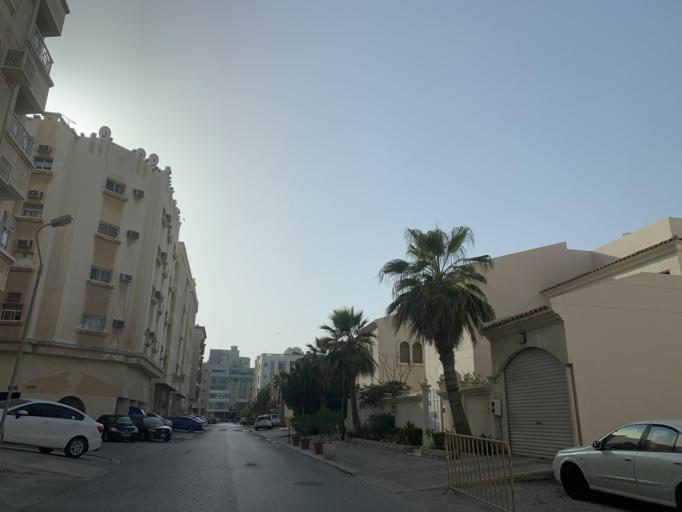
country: BH
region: Manama
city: Manama
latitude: 26.2048
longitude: 50.5838
